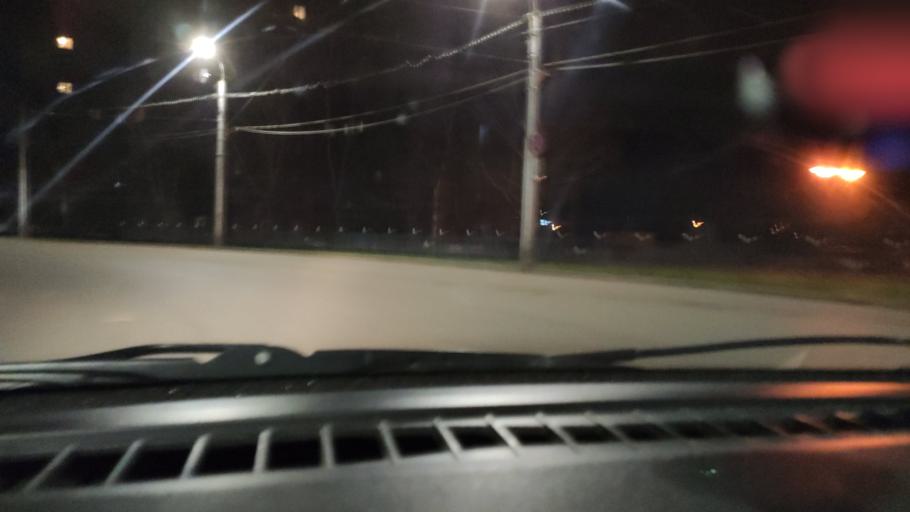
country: RU
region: Bashkortostan
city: Sterlitamak
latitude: 53.6375
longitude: 55.9108
